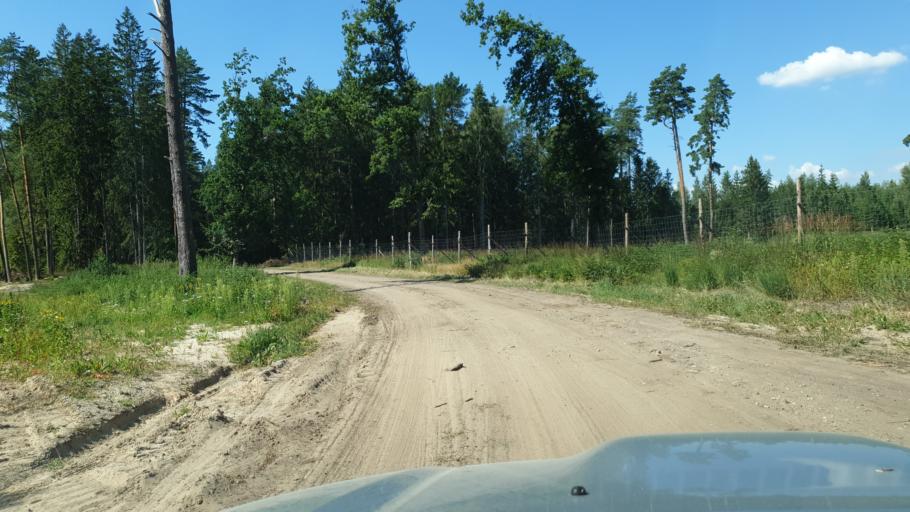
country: LT
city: Sirvintos
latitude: 54.9101
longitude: 24.9361
